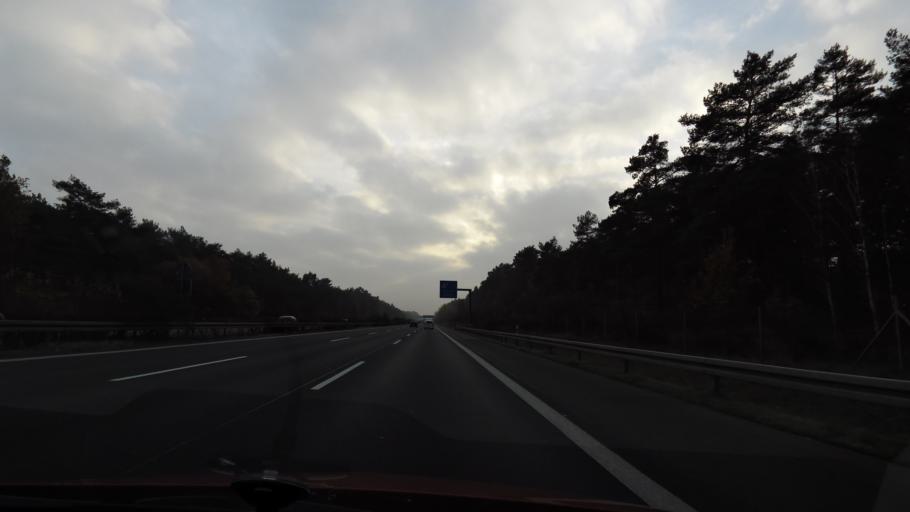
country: DE
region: Brandenburg
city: Borkheide
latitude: 52.2241
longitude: 12.9085
